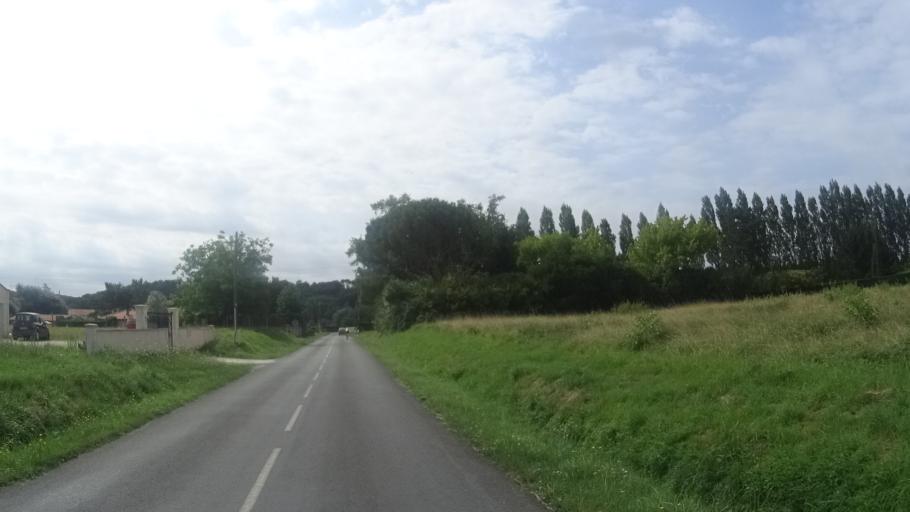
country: FR
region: Aquitaine
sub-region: Departement de la Dordogne
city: Sourzac
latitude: 45.0572
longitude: 0.3947
